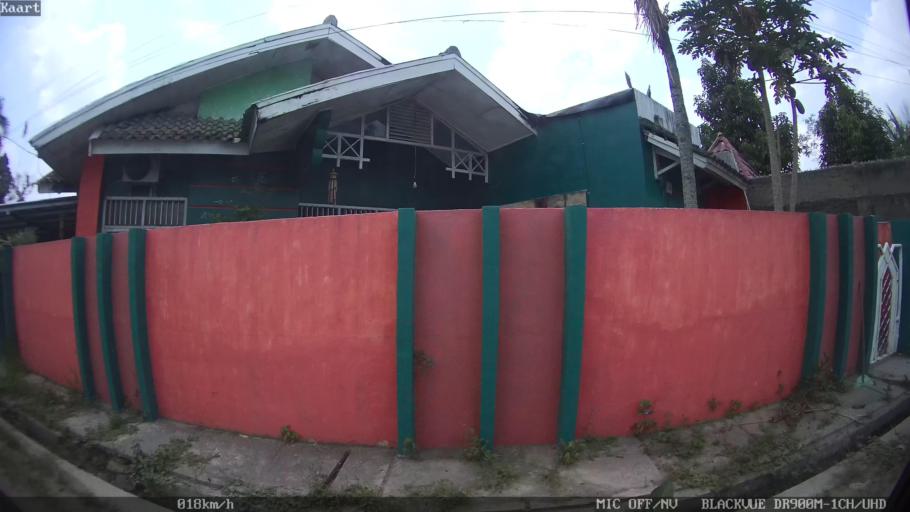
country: ID
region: Lampung
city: Pringsewu
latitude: -5.3513
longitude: 104.9785
